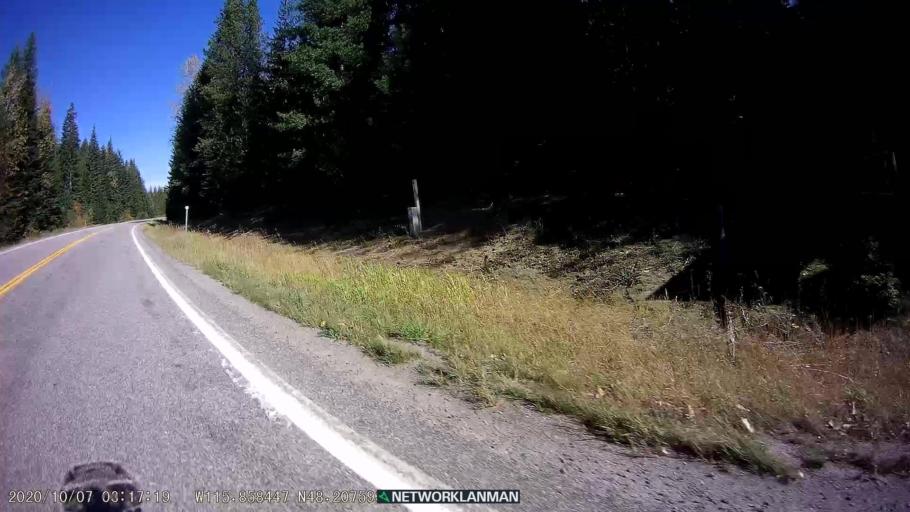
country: US
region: Montana
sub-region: Lincoln County
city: Libby
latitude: 48.2080
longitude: -115.8584
